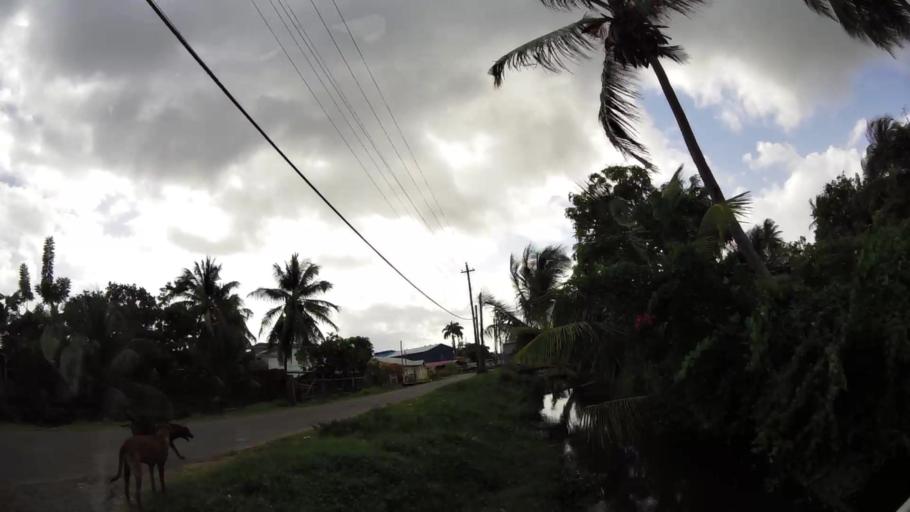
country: GY
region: Demerara-Mahaica
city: Mahaica Village
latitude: 6.6709
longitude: -57.9260
